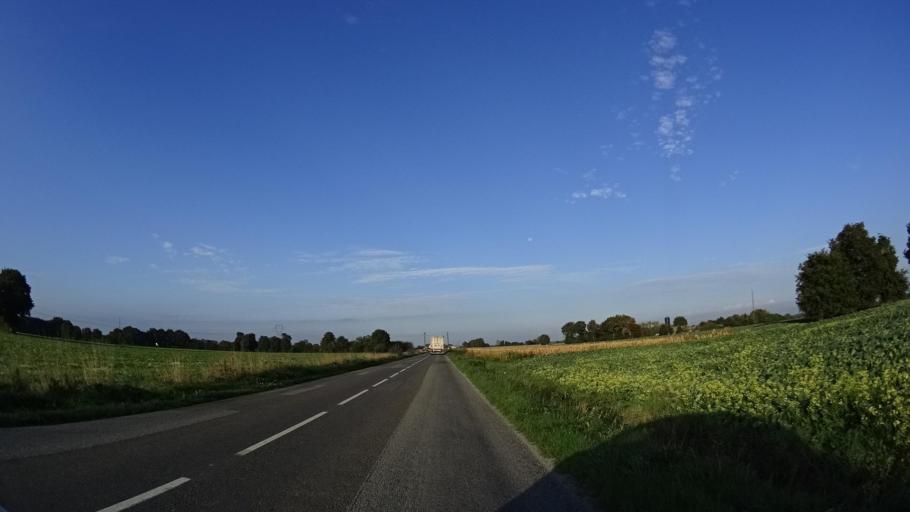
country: FR
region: Brittany
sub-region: Departement d'Ille-et-Vilaine
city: Quedillac
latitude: 48.2579
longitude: -2.1063
